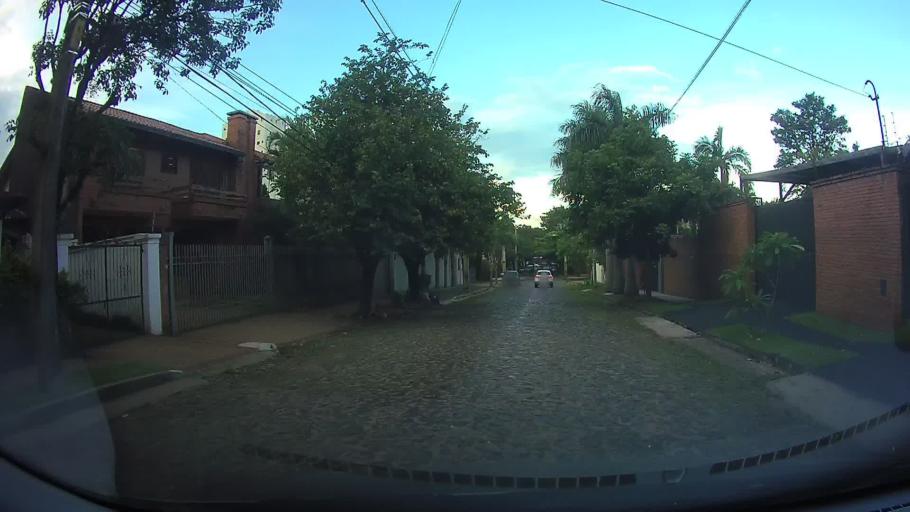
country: PY
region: Asuncion
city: Asuncion
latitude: -25.2786
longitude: -57.5659
